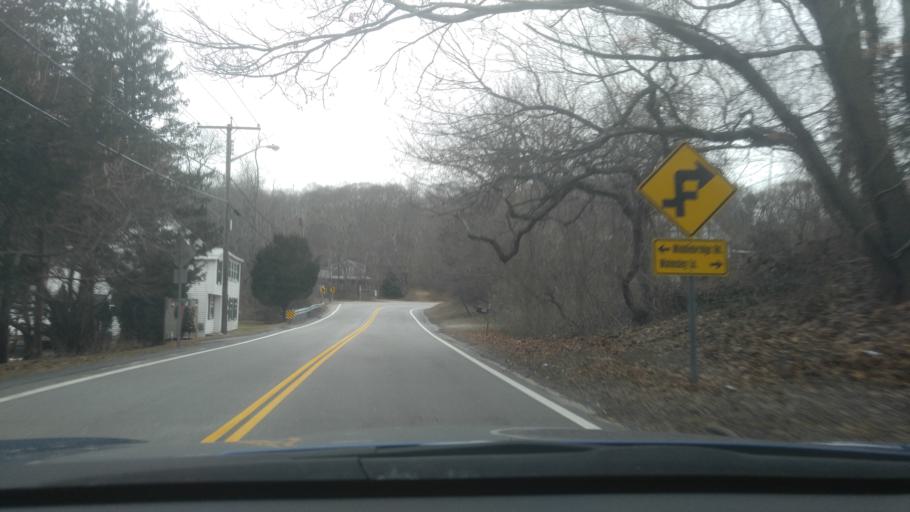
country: US
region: Rhode Island
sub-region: Washington County
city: Narragansett Pier
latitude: 41.4882
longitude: -71.4479
